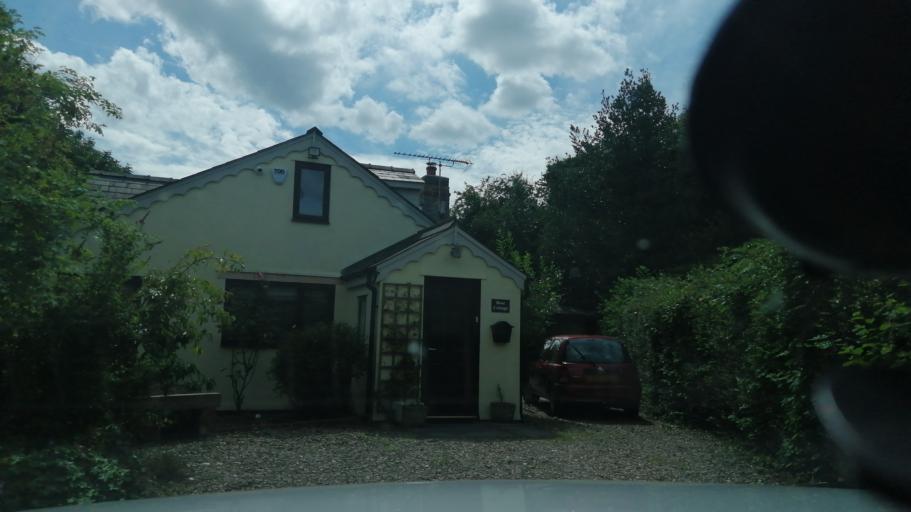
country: GB
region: England
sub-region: Herefordshire
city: Thruxton
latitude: 52.0169
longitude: -2.7973
